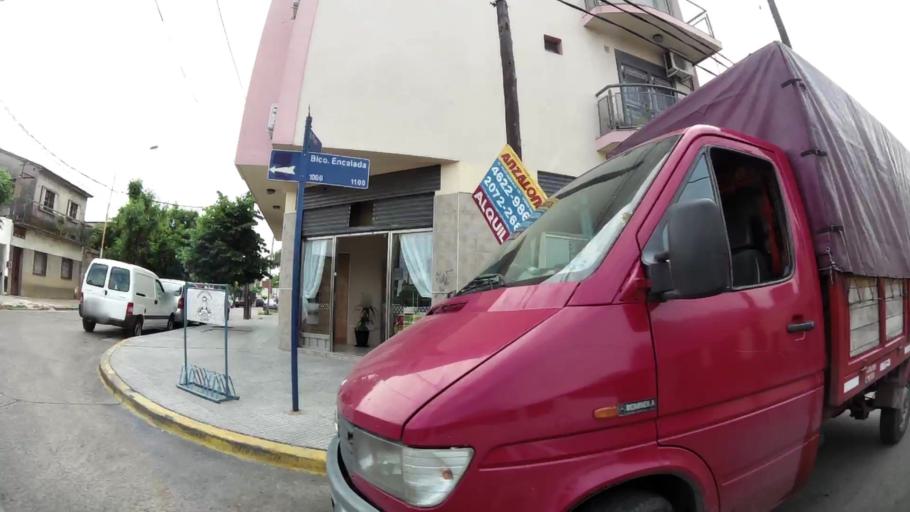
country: AR
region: Buenos Aires F.D.
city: Villa Lugano
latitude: -34.6842
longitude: -58.4988
